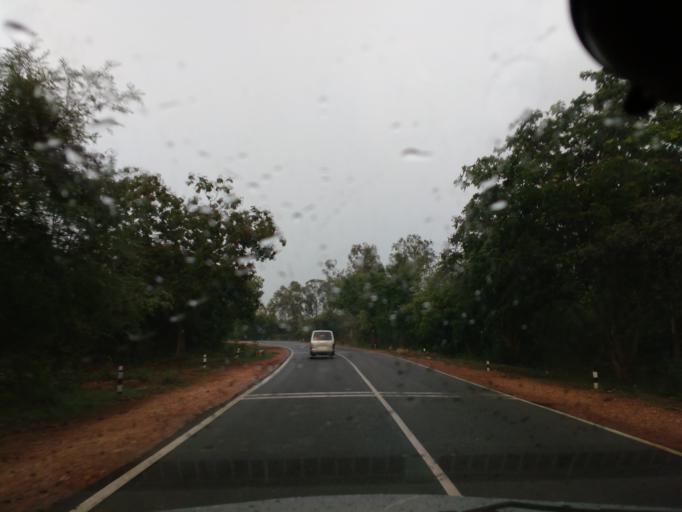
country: IN
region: Karnataka
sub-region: Tumkur
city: Tiptur
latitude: 13.2970
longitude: 76.5874
